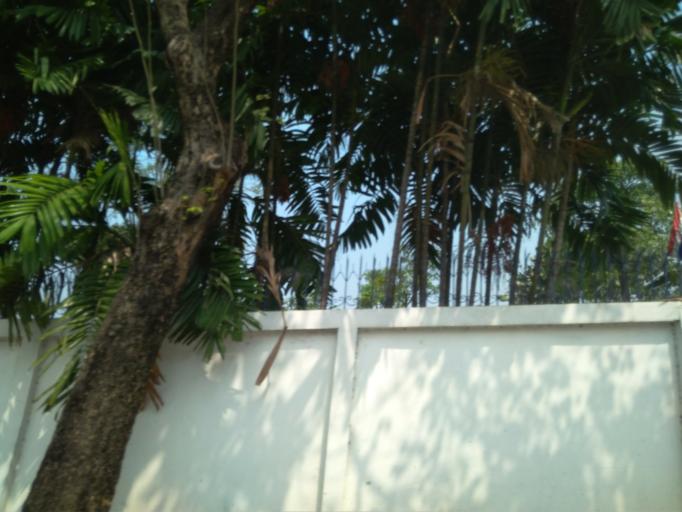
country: TH
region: Bangkok
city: Taling Chan
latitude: 13.7784
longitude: 100.4494
